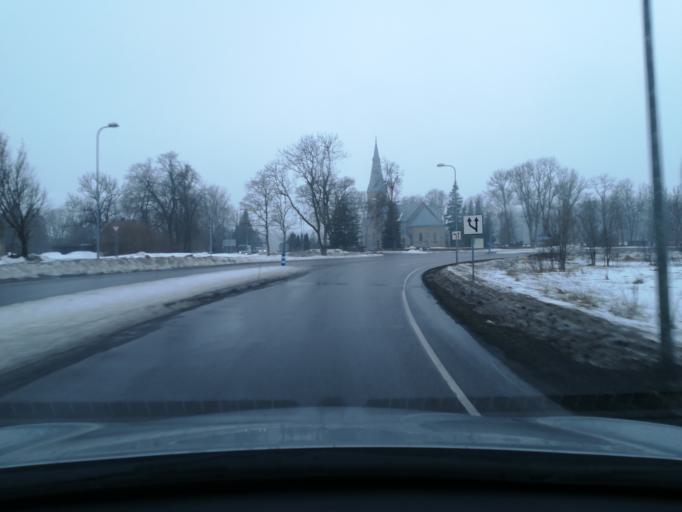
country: EE
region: Harju
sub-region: Rae vald
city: Jueri
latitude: 59.3594
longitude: 24.9256
